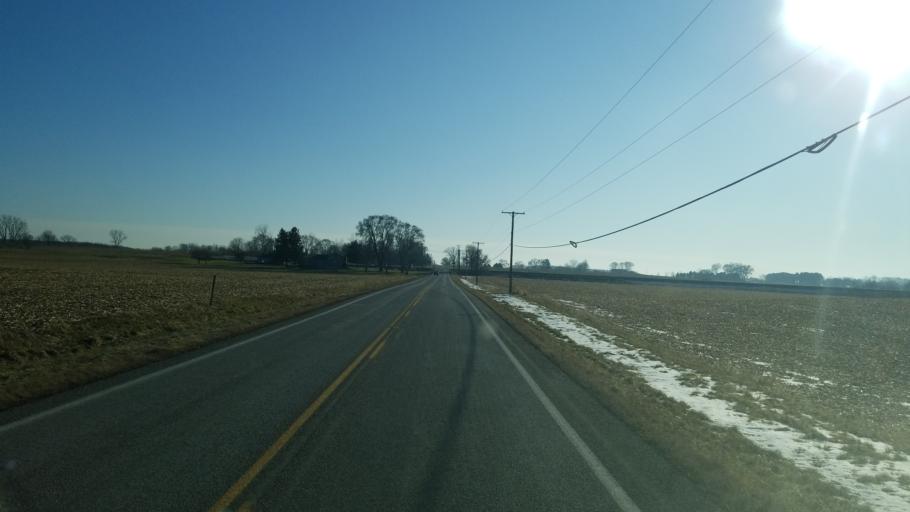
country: US
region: Ohio
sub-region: Sandusky County
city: Clyde
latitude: 41.2665
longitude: -82.9752
